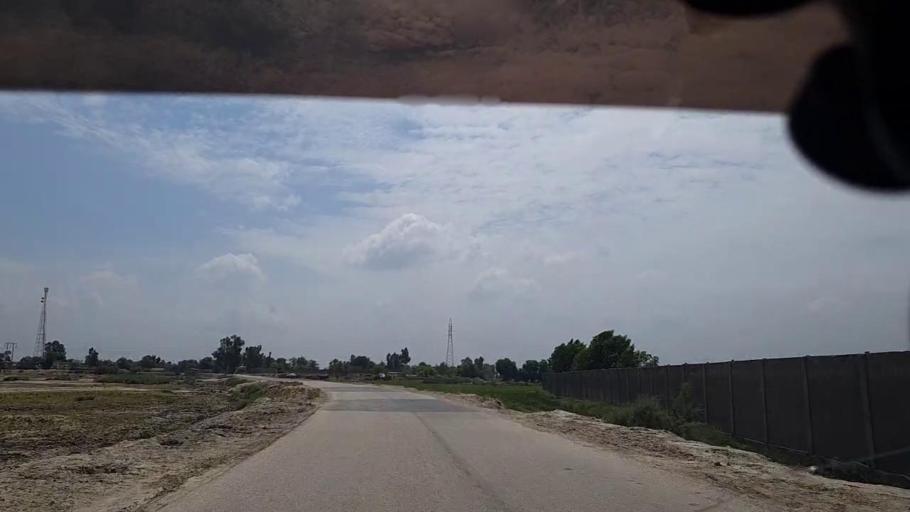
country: PK
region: Sindh
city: Ghauspur
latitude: 28.0909
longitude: 68.9607
